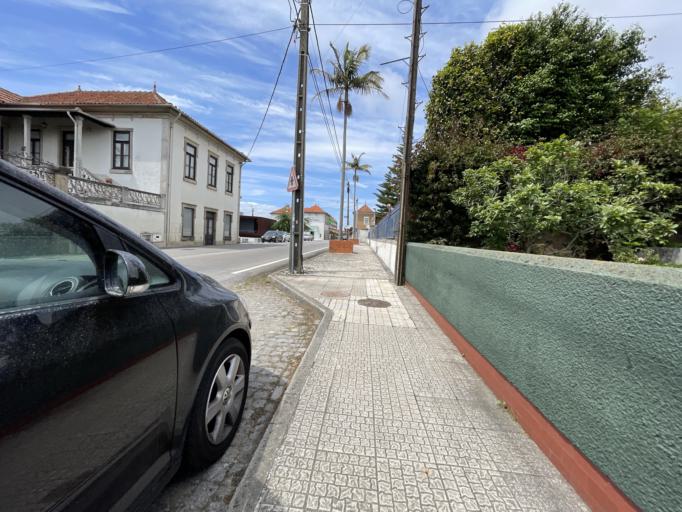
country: PT
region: Aveiro
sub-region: Ovar
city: Cortegaca
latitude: 40.9464
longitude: -8.6229
